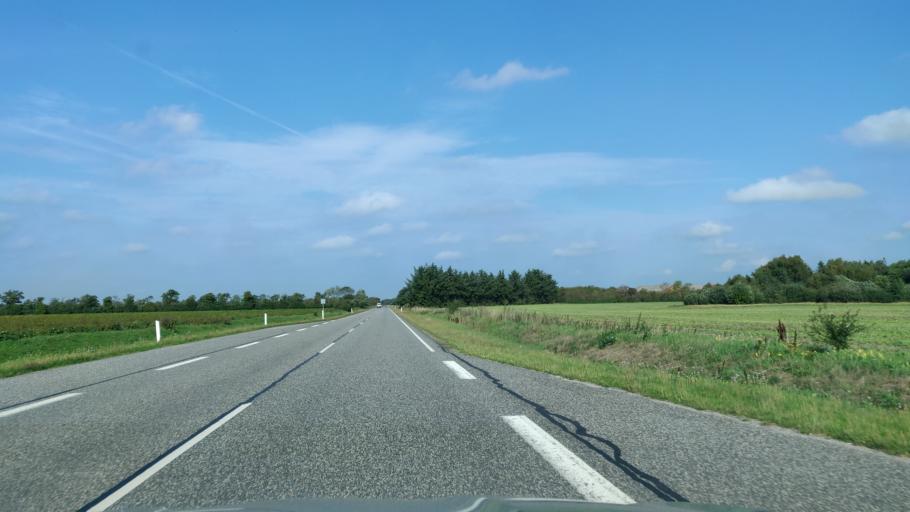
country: DK
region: Central Jutland
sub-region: Herning Kommune
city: Sunds
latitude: 56.2504
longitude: 9.0582
